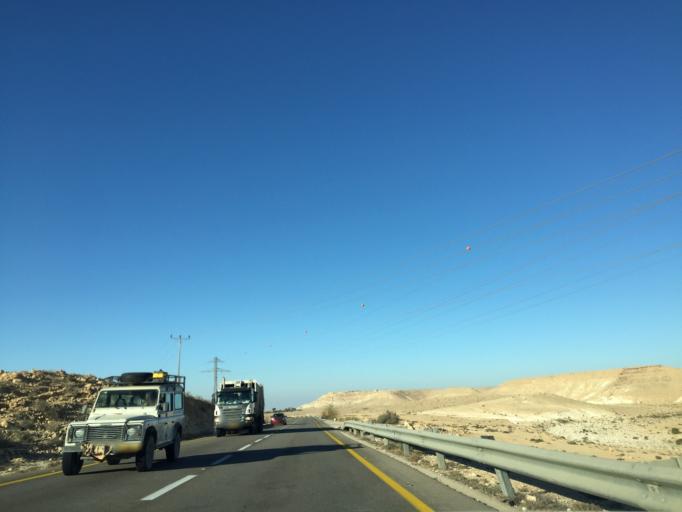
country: IL
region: Southern District
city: Midreshet Ben-Gurion
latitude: 30.7687
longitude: 34.7718
